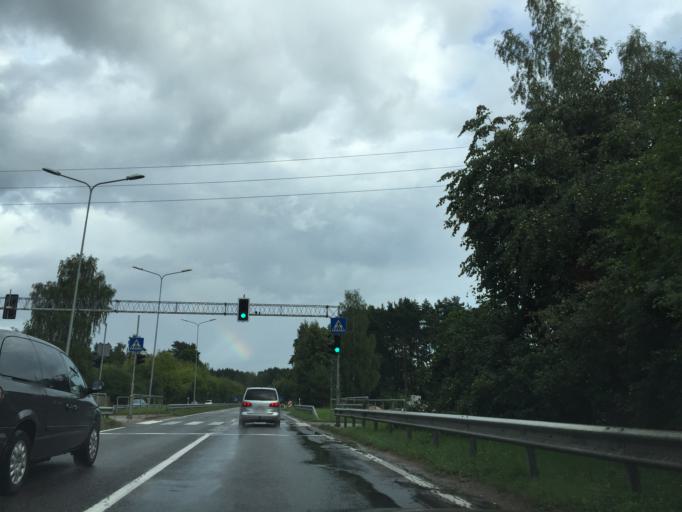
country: LV
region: Babite
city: Pinki
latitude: 56.9595
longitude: 23.9530
